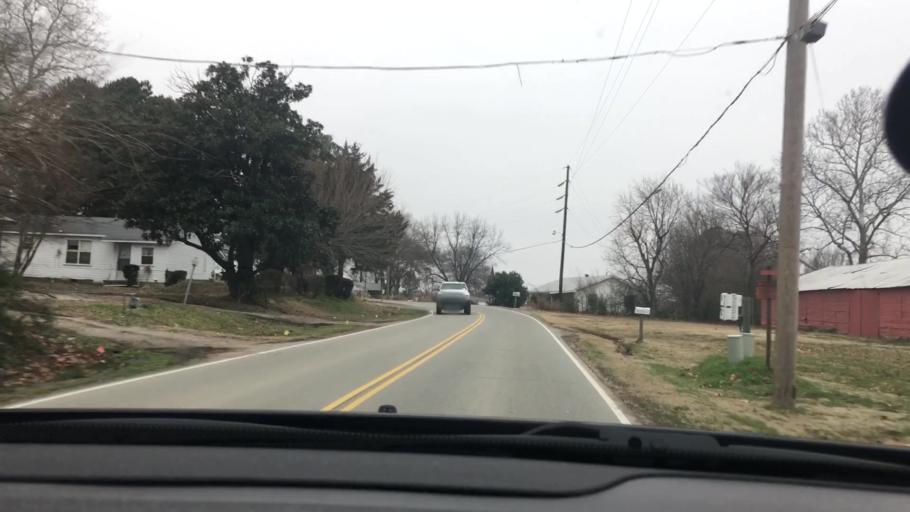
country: US
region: Oklahoma
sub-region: Coal County
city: Coalgate
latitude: 34.5408
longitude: -96.2268
